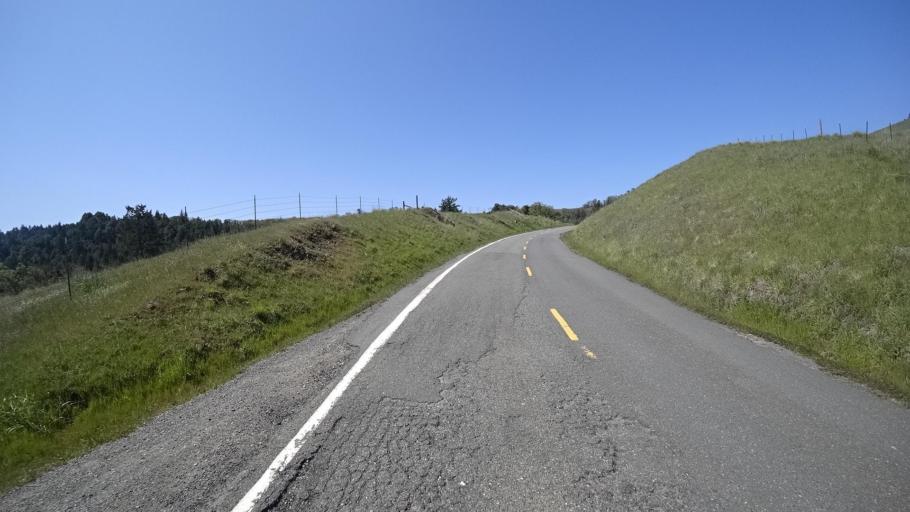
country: US
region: California
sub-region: Humboldt County
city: Redway
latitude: 40.1039
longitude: -123.6779
